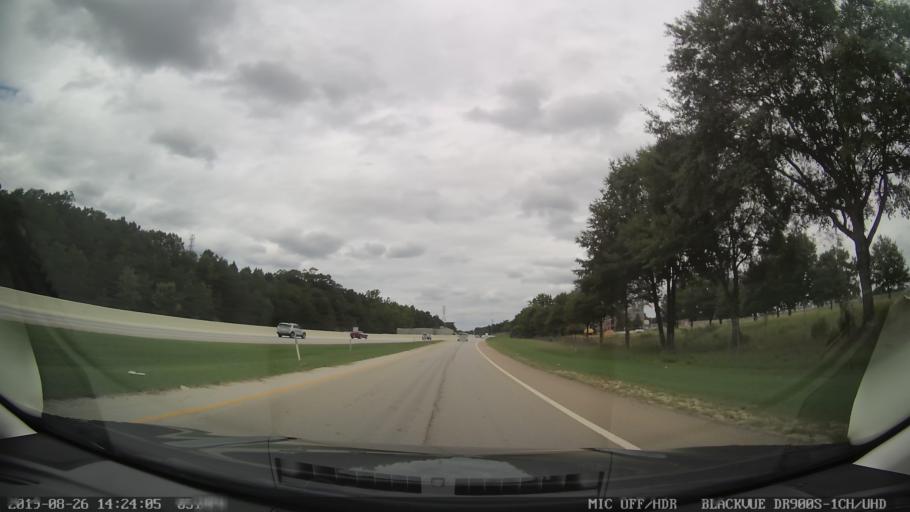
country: US
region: South Carolina
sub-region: Greenville County
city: Mauldin
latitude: 34.7922
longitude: -82.2799
